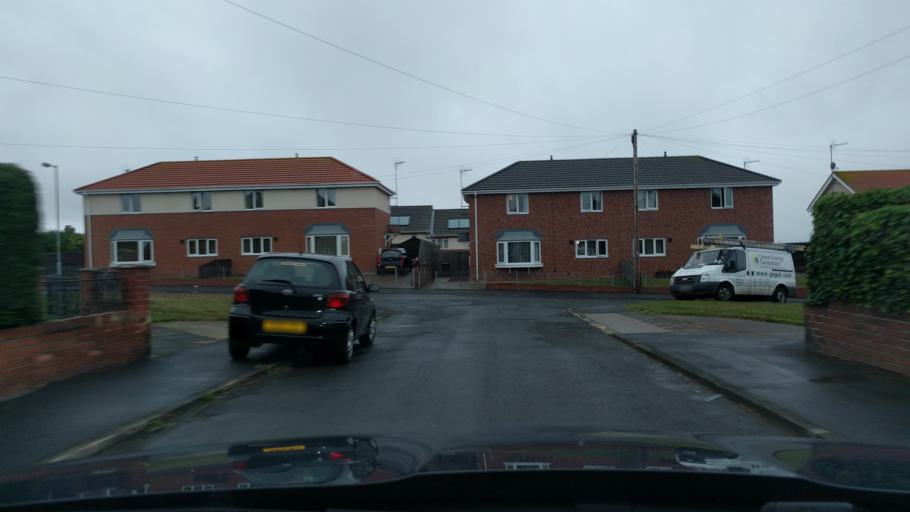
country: GB
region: England
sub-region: Northumberland
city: Bedlington
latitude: 55.1345
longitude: -1.5795
